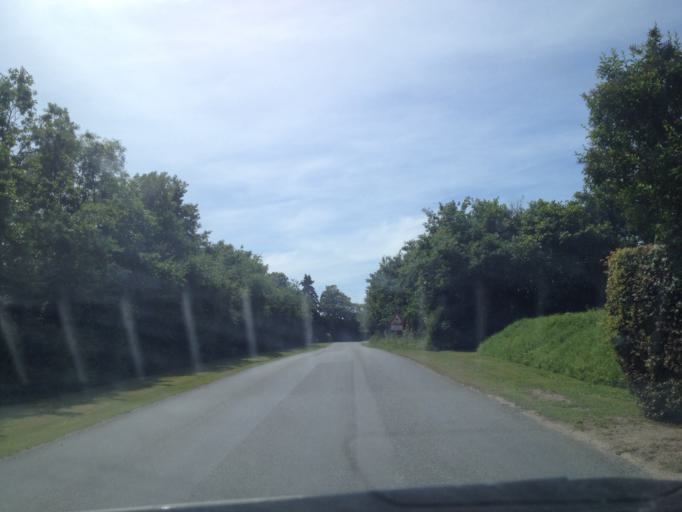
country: DK
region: Central Jutland
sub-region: Samso Kommune
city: Tranebjerg
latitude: 55.8406
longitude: 10.6155
